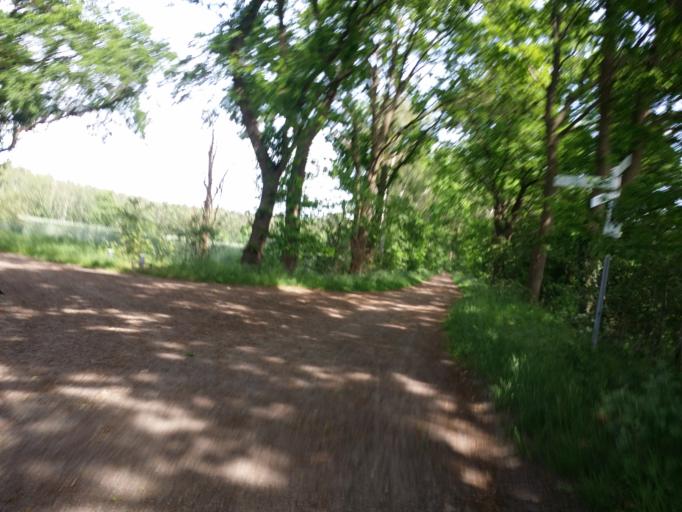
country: DE
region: Lower Saxony
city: Syke
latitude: 52.9478
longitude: 8.8619
